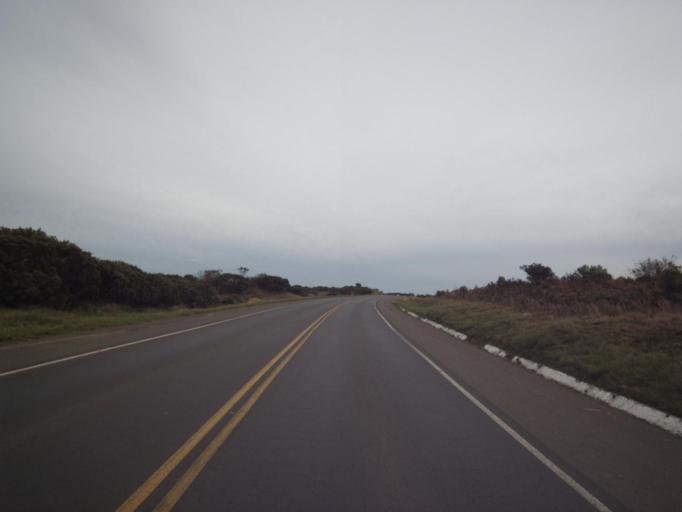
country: BR
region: Parana
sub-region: Palmas
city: Palmas
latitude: -26.6312
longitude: -51.5043
